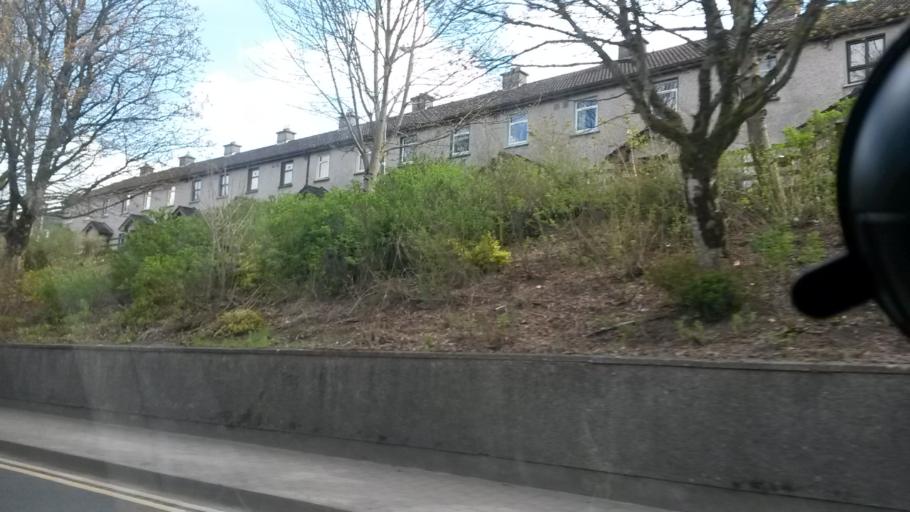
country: IE
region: Ulster
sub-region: An Cabhan
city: Cavan
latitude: 53.9856
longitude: -7.3595
